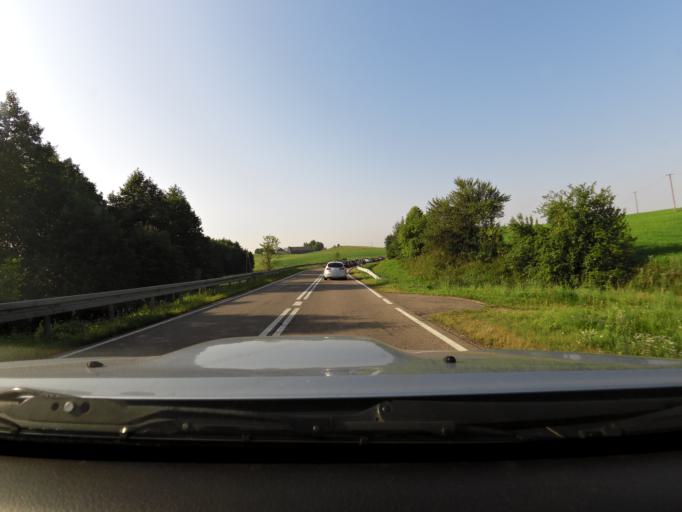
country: PL
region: Podlasie
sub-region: Powiat sejnenski
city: Sejny
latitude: 54.1137
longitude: 23.4236
